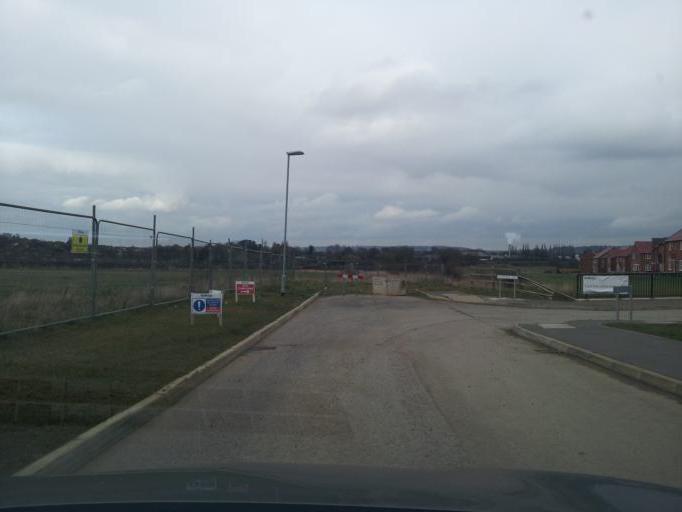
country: GB
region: England
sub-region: Lincolnshire
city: Great Gonerby
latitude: 52.9204
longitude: -0.6620
